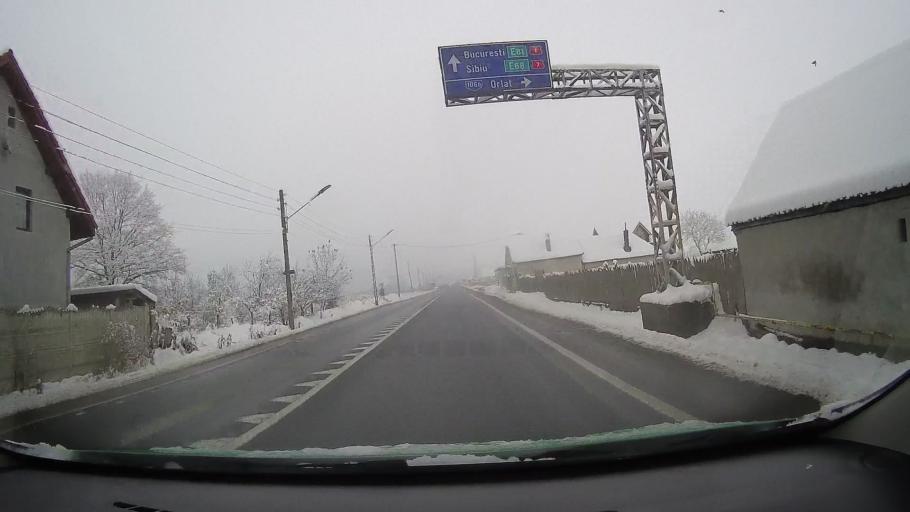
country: RO
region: Sibiu
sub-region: Comuna Orlat
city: Orlat
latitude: 45.7830
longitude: 23.9418
